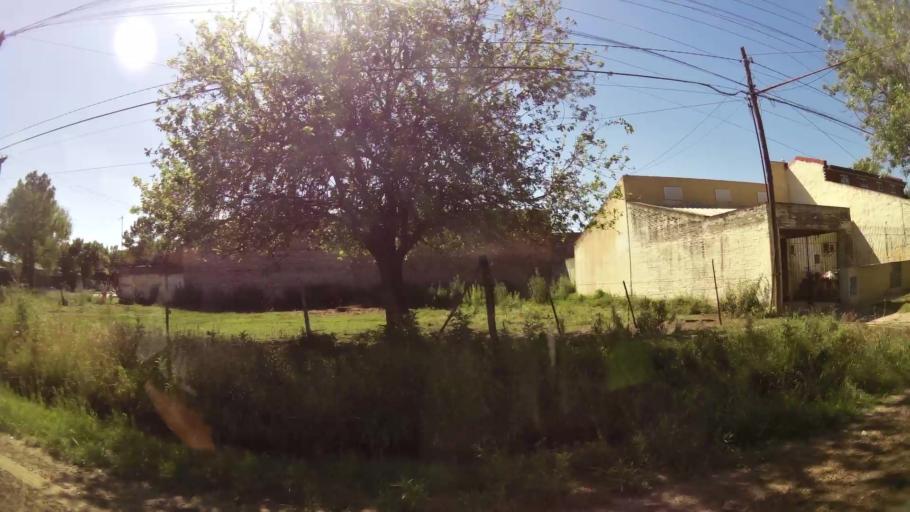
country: AR
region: Santa Fe
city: Esperanza
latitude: -31.4615
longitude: -60.9321
